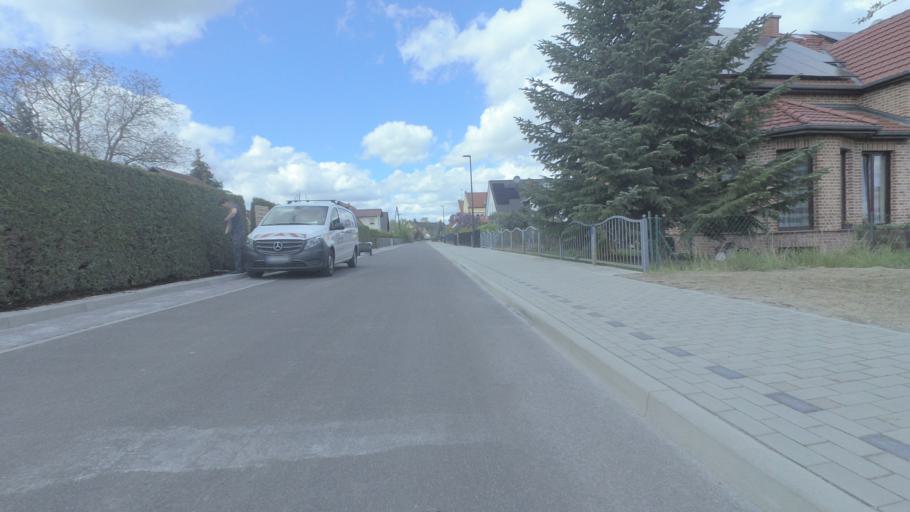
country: DE
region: Brandenburg
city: Ludwigsfelde
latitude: 52.2935
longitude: 13.2598
